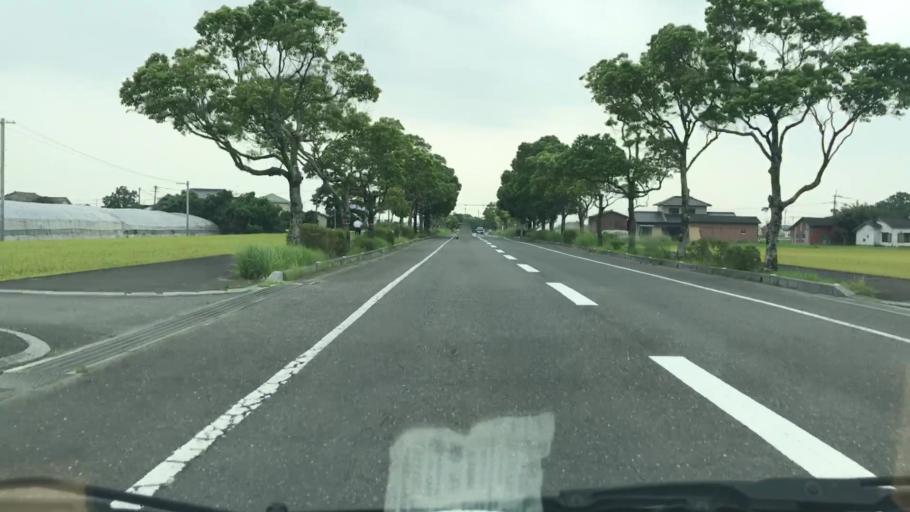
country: JP
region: Saga Prefecture
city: Saga-shi
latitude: 33.2265
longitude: 130.3063
